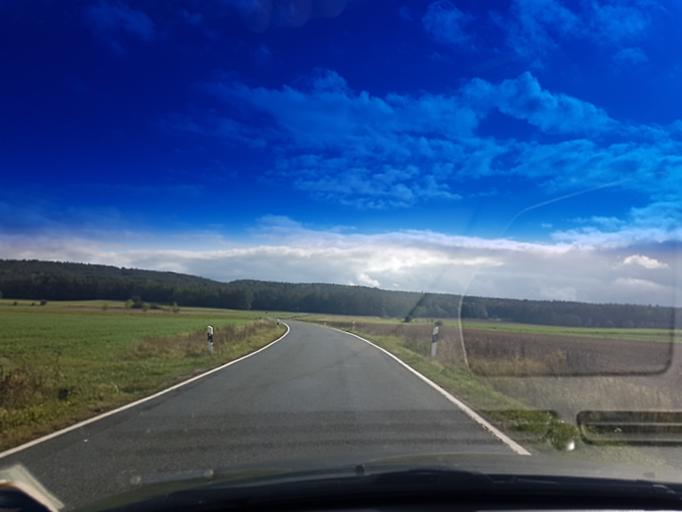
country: DE
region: Bavaria
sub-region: Upper Franconia
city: Frensdorf
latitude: 49.7866
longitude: 10.8866
